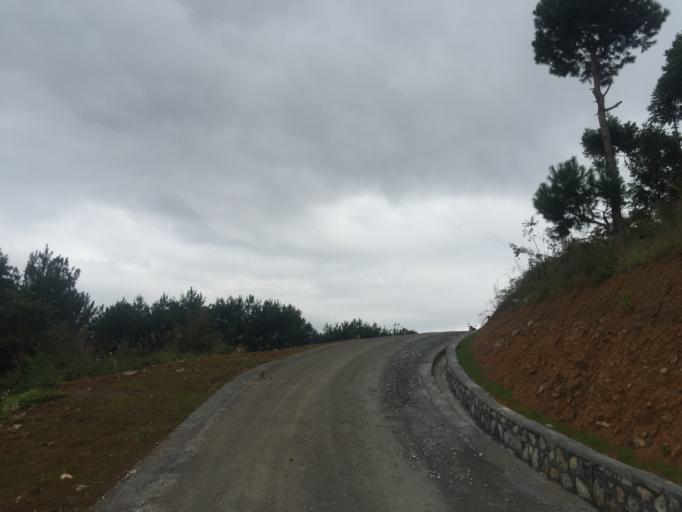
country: CN
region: Guizhou Sheng
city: Chaodi
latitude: 27.9866
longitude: 108.2178
